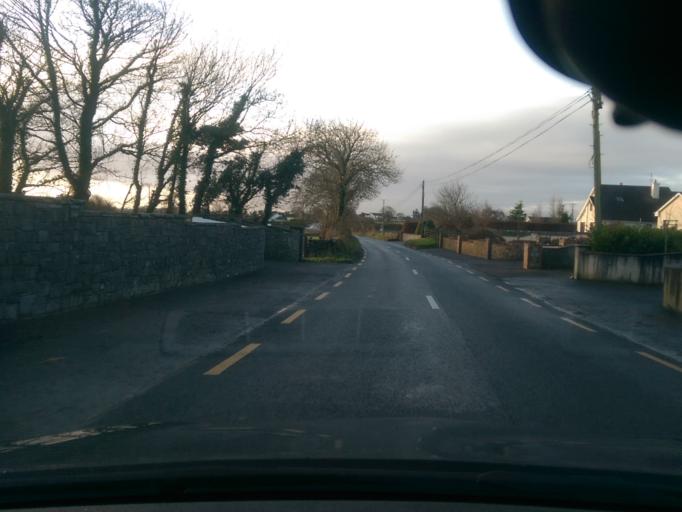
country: IE
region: Connaught
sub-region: County Galway
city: Athenry
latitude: 53.3248
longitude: -8.7261
